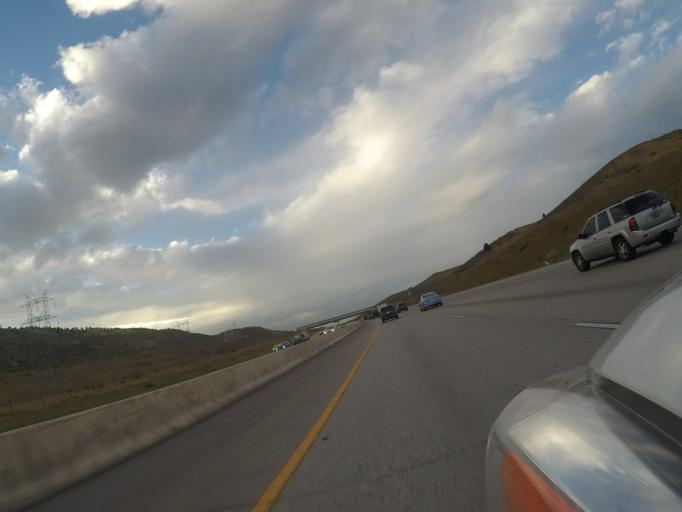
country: US
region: Colorado
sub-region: Jefferson County
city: West Pleasant View
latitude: 39.6923
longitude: -105.1883
